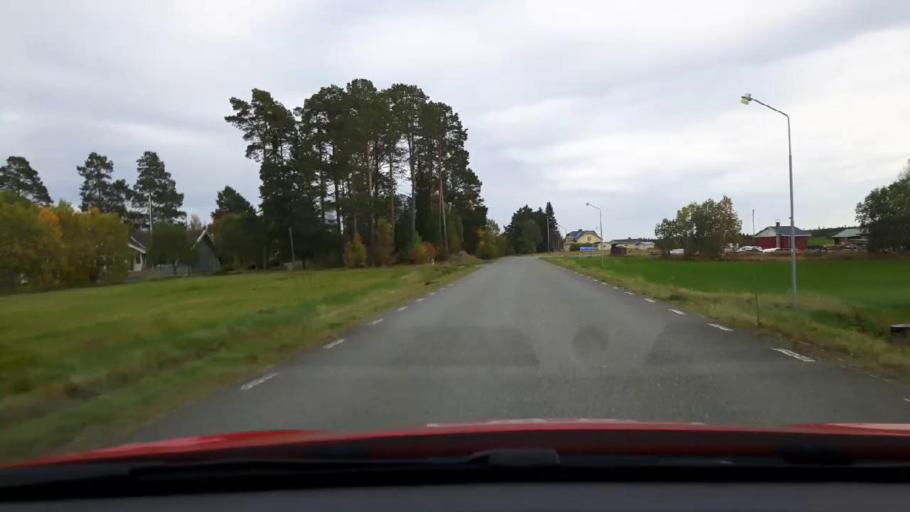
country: SE
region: Jaemtland
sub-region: Krokoms Kommun
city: Krokom
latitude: 63.2270
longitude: 14.1322
